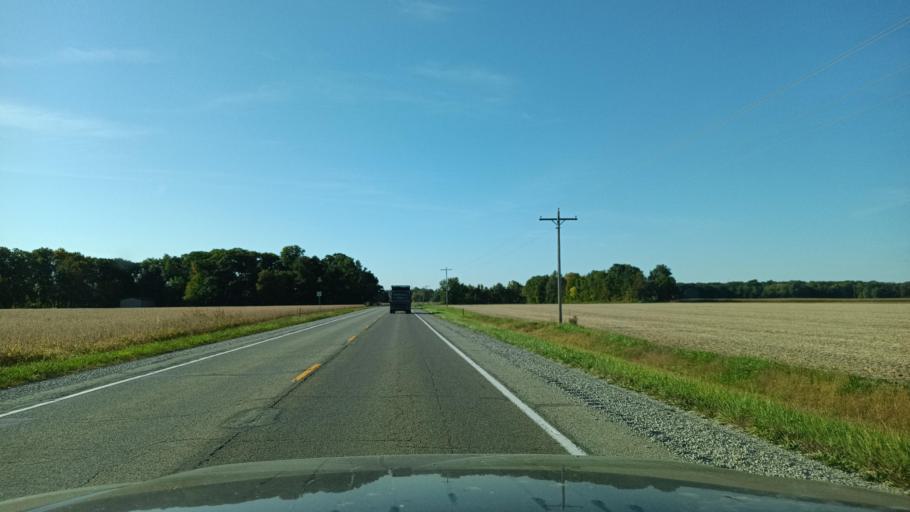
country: US
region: Illinois
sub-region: Clark County
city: Marshall
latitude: 39.4512
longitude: -87.6821
